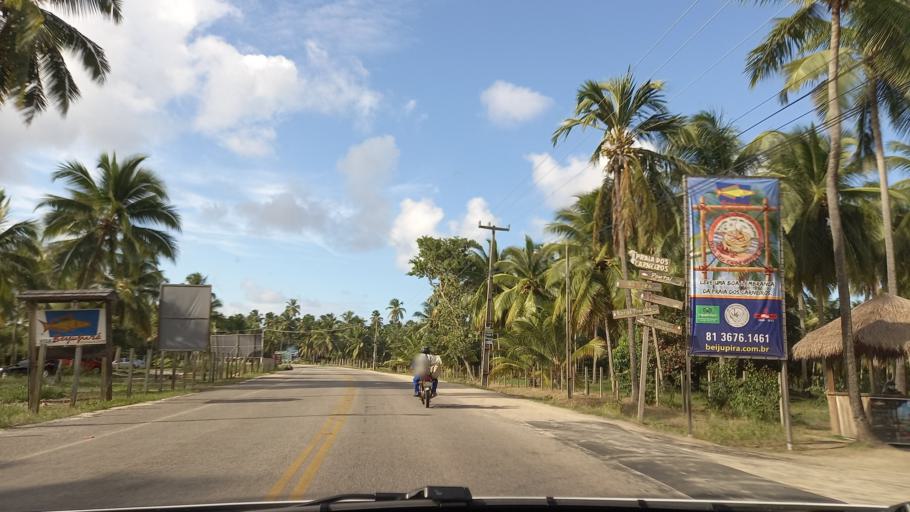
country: BR
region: Pernambuco
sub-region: Tamandare
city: Tamandare
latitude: -8.7072
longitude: -35.0874
